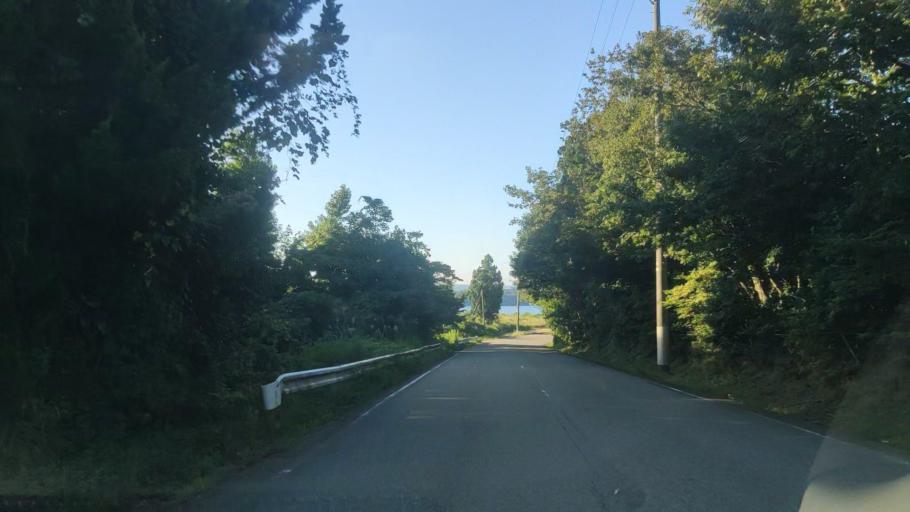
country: JP
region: Ishikawa
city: Nanao
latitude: 37.1294
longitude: 136.9315
